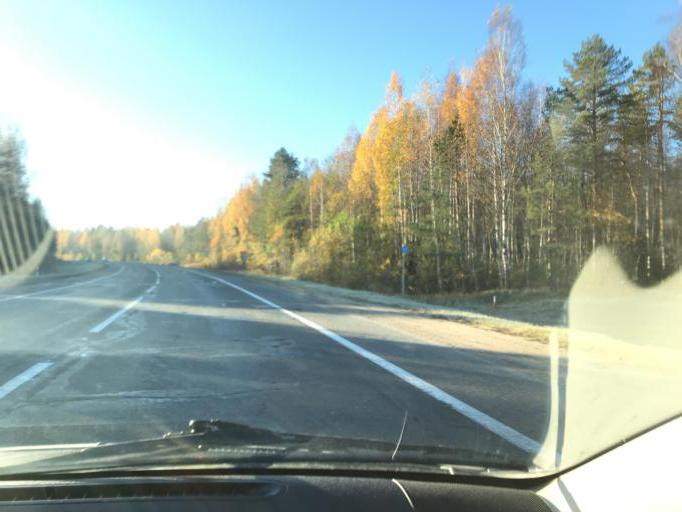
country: BY
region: Vitebsk
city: Vitebsk
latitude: 54.9001
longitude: 30.3768
